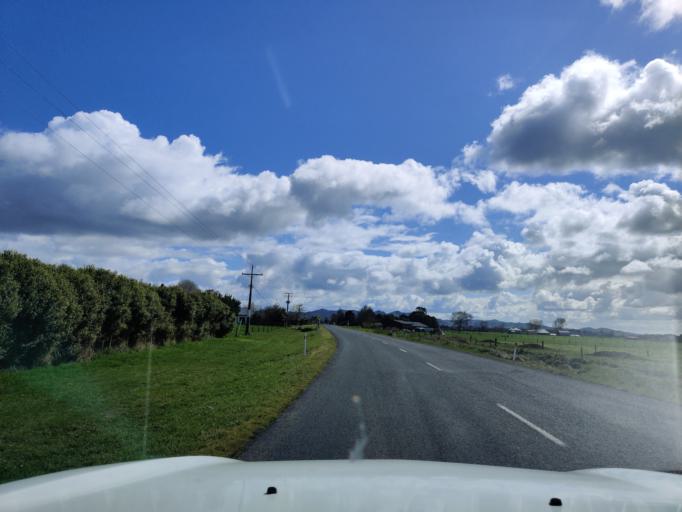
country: NZ
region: Waikato
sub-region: Waikato District
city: Ngaruawahia
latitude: -37.5873
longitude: 175.2873
